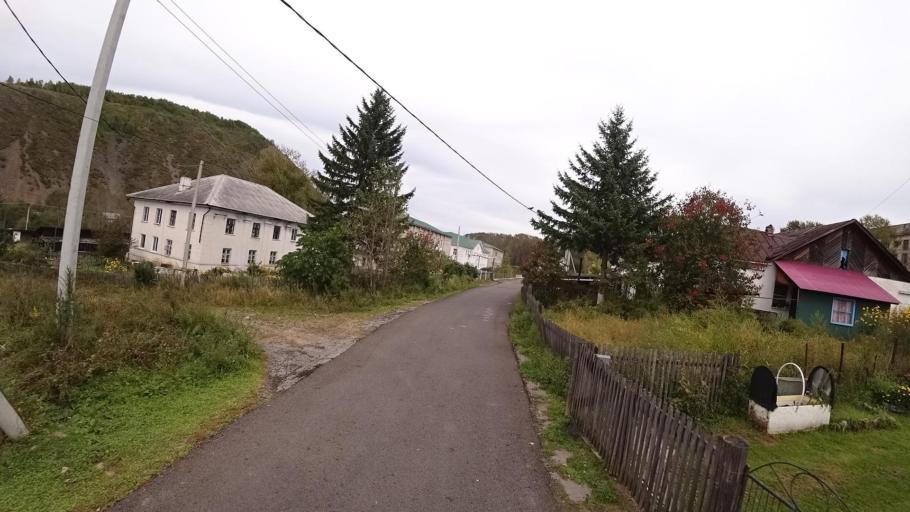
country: RU
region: Jewish Autonomous Oblast
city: Khingansk
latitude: 49.1272
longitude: 131.1911
